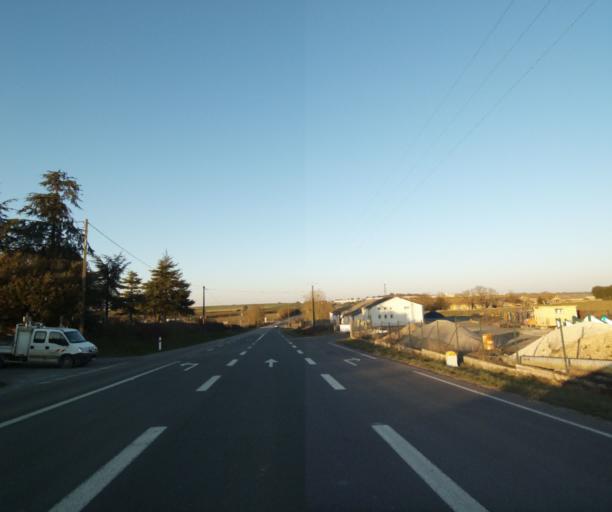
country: FR
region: Poitou-Charentes
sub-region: Departement des Deux-Sevres
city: Niort
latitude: 46.3532
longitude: -0.4397
